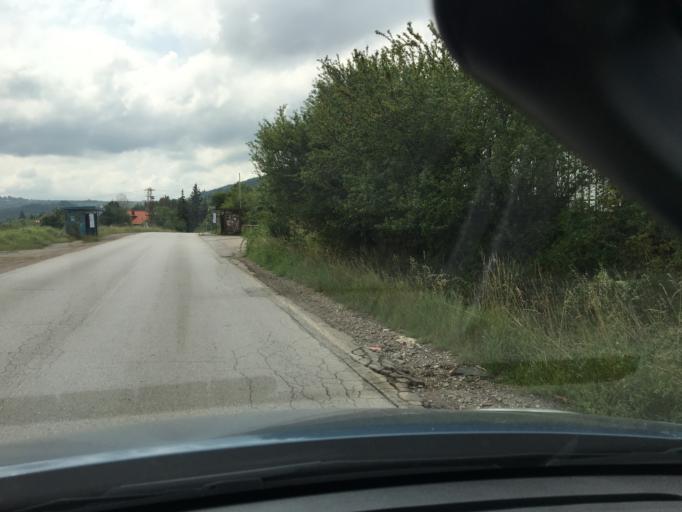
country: BG
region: Sofia-Capital
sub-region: Stolichna Obshtina
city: Sofia
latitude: 42.6144
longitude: 23.3635
